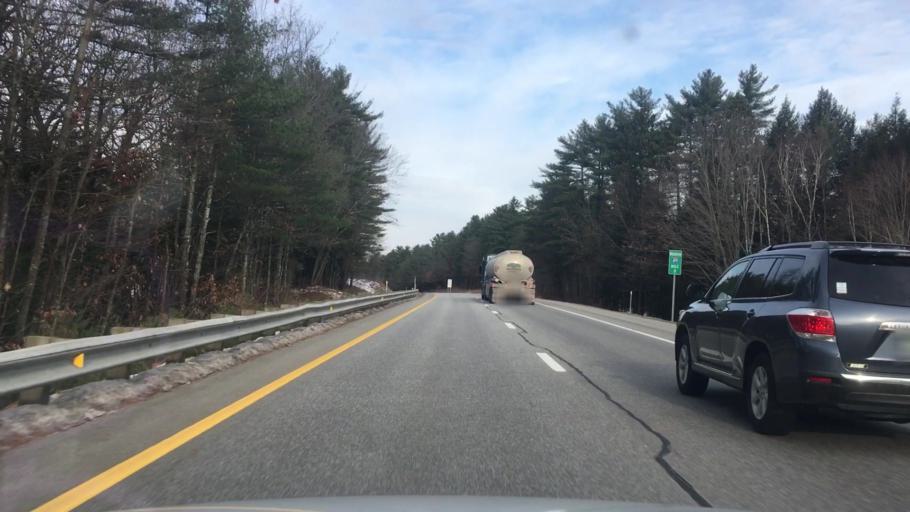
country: US
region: New Hampshire
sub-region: Merrimack County
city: Contoocook
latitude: 43.2100
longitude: -71.7130
